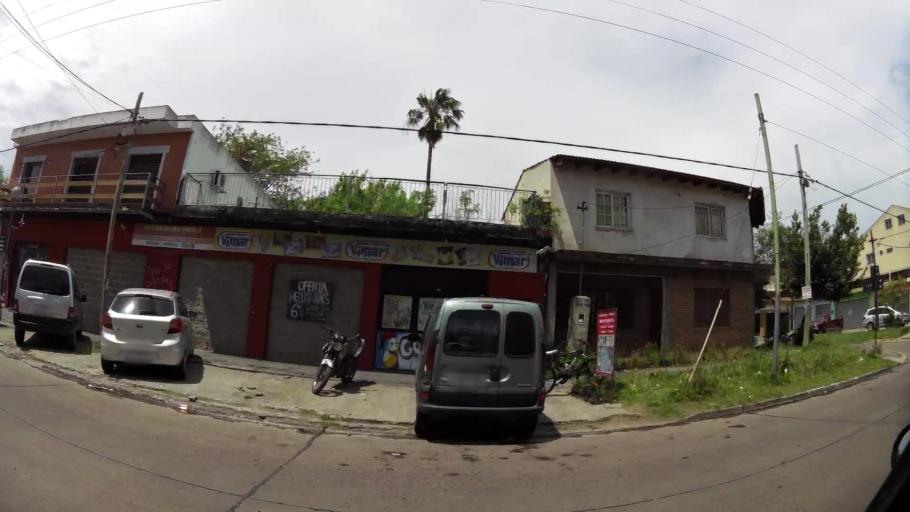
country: AR
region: Buenos Aires
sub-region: Partido de Quilmes
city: Quilmes
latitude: -34.7685
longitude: -58.2397
